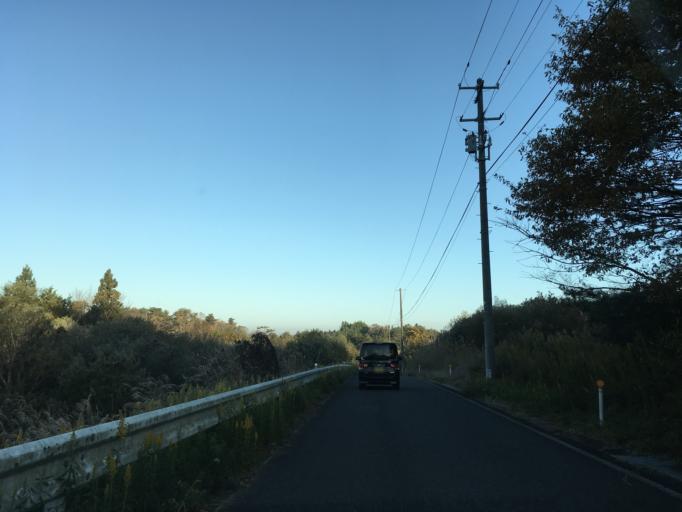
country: JP
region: Iwate
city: Ichinoseki
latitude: 38.7902
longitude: 141.2124
